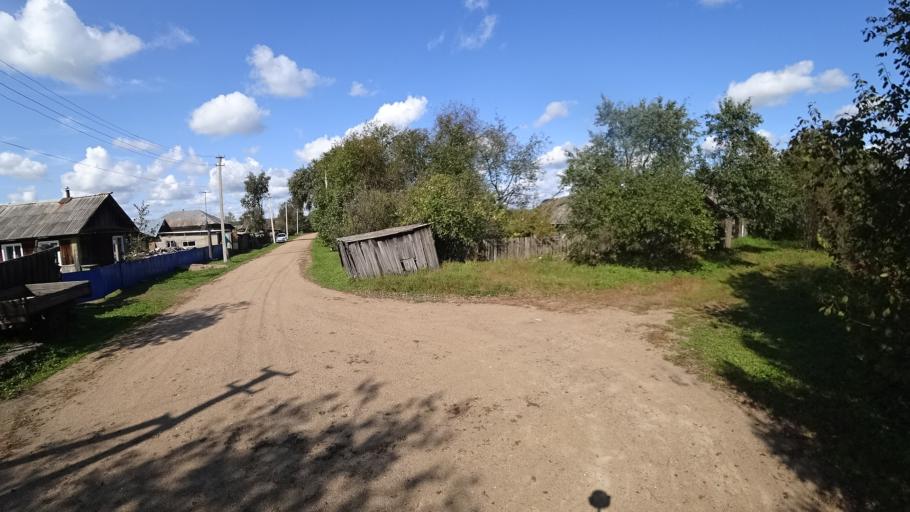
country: RU
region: Amur
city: Arkhara
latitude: 49.4000
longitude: 130.1500
